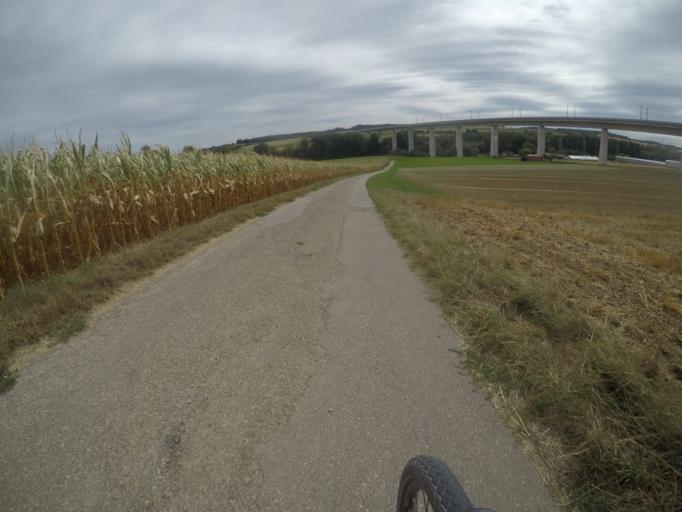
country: DE
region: Baden-Wuerttemberg
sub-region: Regierungsbezirk Stuttgart
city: Oberriexingen
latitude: 48.9269
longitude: 8.9982
